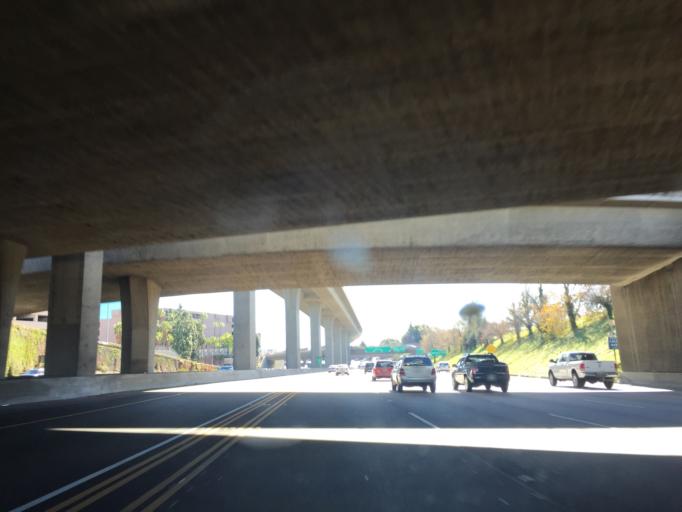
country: US
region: California
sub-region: Orange County
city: Tustin
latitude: 33.7485
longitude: -117.8435
